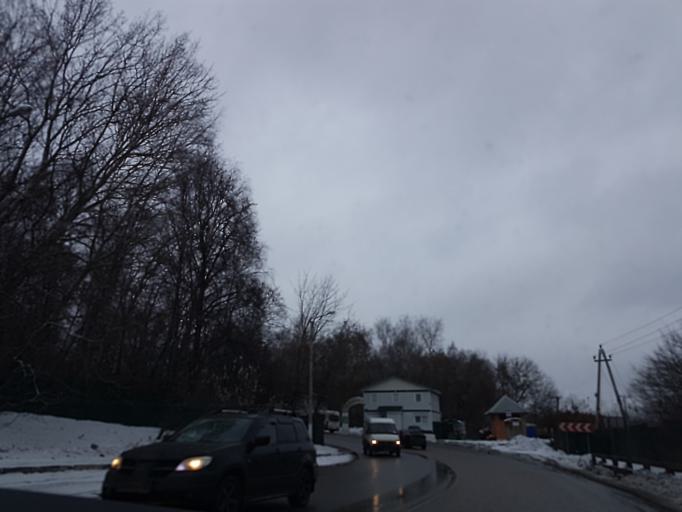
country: RU
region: Moskovskaya
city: Pavshino
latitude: 55.8197
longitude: 37.3587
